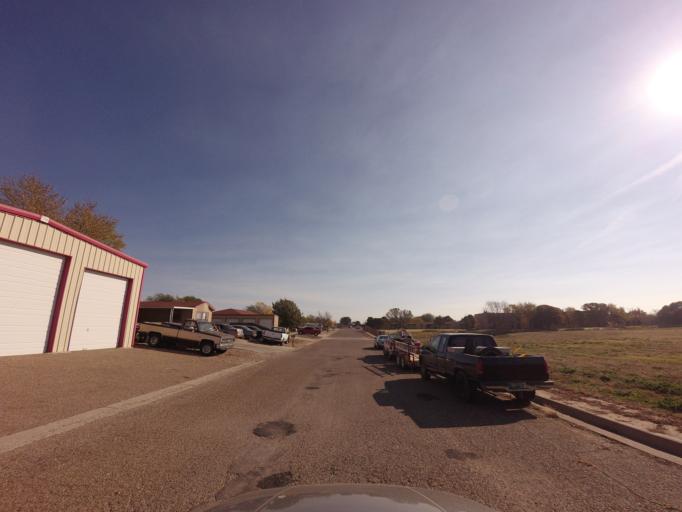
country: US
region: New Mexico
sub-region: Curry County
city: Clovis
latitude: 34.4083
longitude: -103.1770
